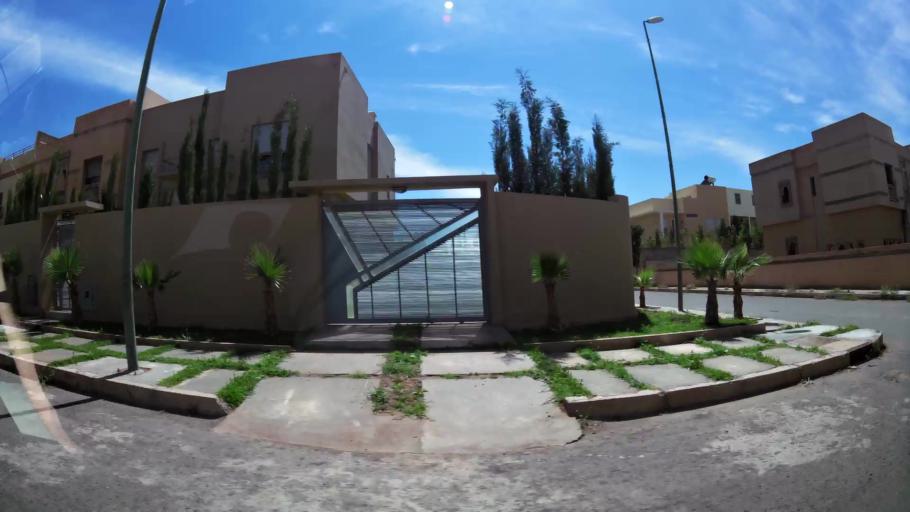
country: MA
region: Marrakech-Tensift-Al Haouz
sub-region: Marrakech
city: Marrakesh
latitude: 31.6510
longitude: -8.0720
